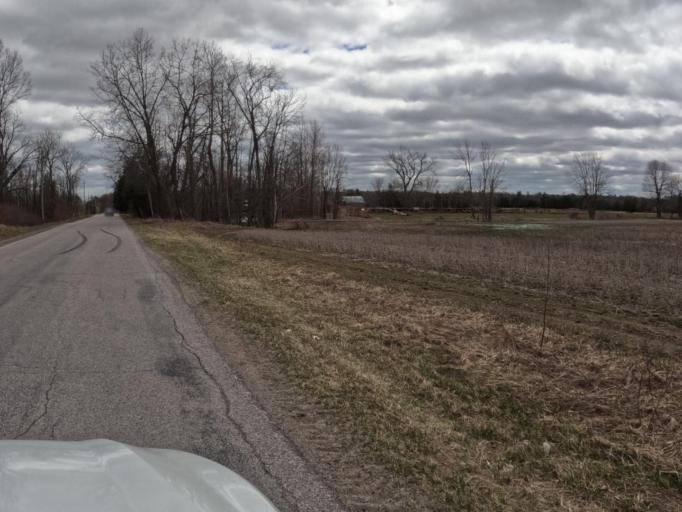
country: CA
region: Ontario
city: Norfolk County
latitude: 42.7973
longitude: -80.3630
